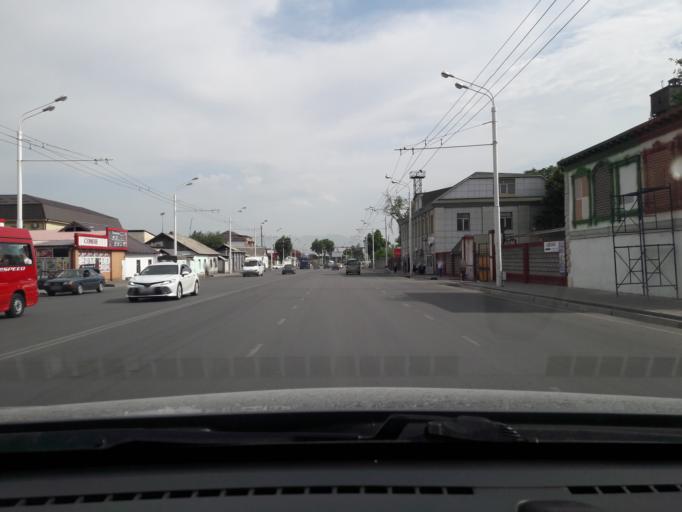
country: TJ
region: Dushanbe
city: Dushanbe
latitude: 38.5428
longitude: 68.7553
